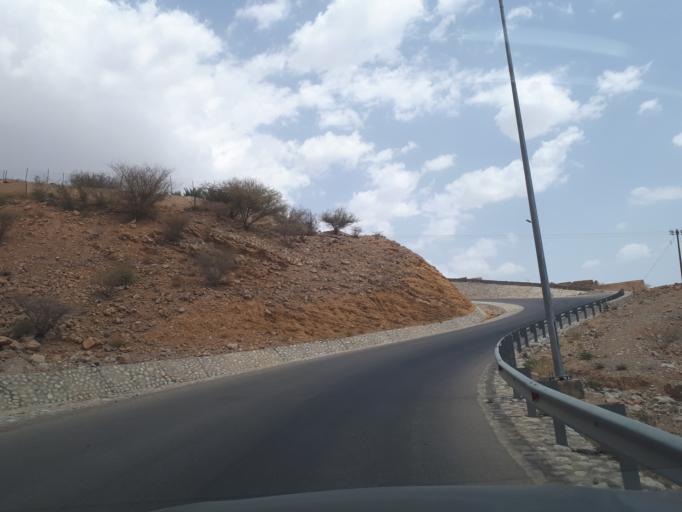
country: OM
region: Ash Sharqiyah
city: Badiyah
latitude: 22.6066
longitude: 59.0838
